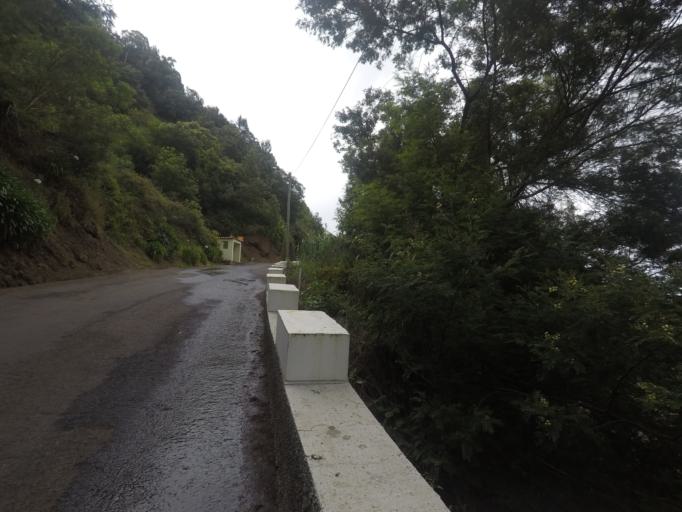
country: PT
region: Madeira
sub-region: Santana
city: Santana
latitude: 32.7574
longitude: -16.8789
